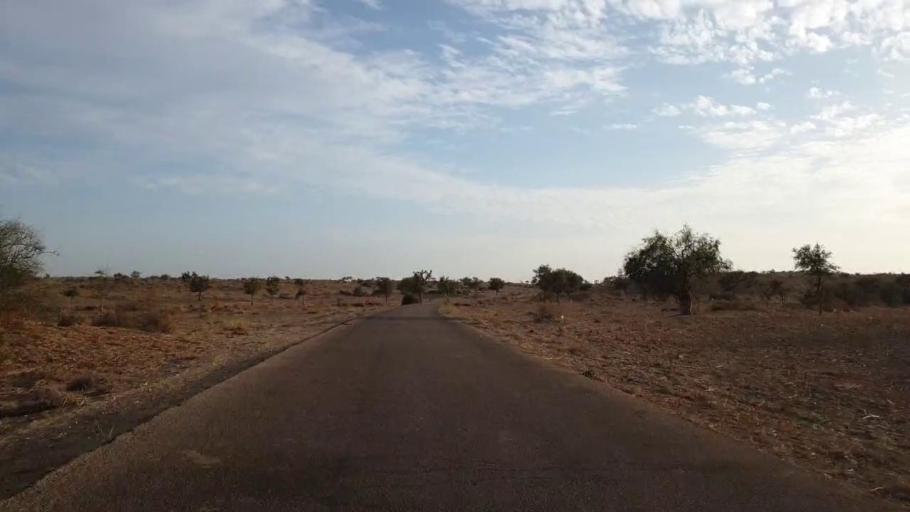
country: PK
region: Sindh
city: Umarkot
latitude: 25.1428
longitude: 70.0129
